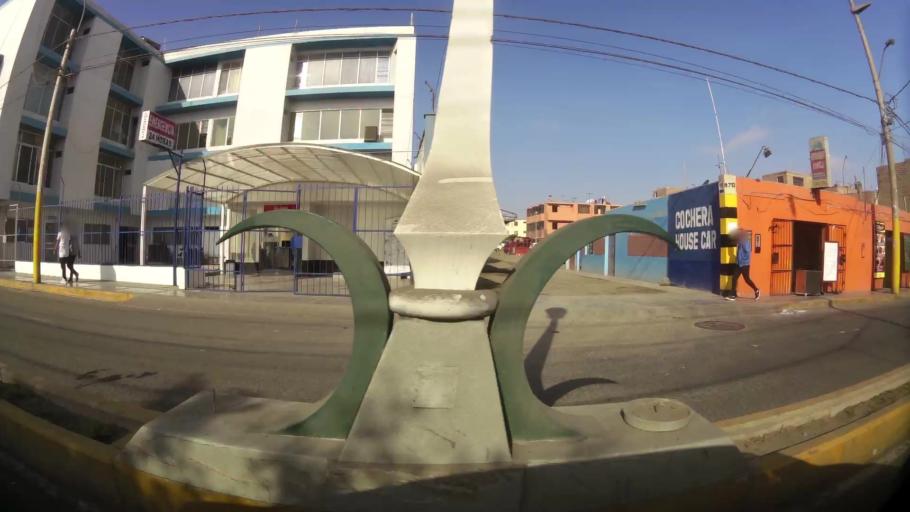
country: PE
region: Lima
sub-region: Huaura
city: Huacho
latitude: -11.1118
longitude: -77.6101
